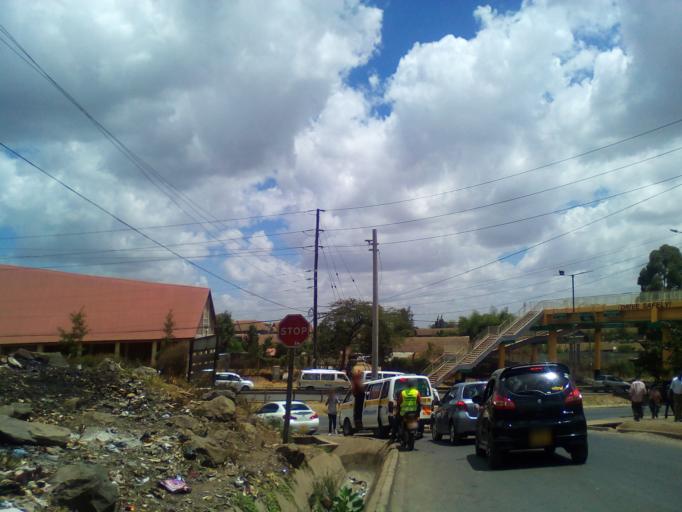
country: KE
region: Nairobi Area
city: Nairobi
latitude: -1.3142
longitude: 36.8074
